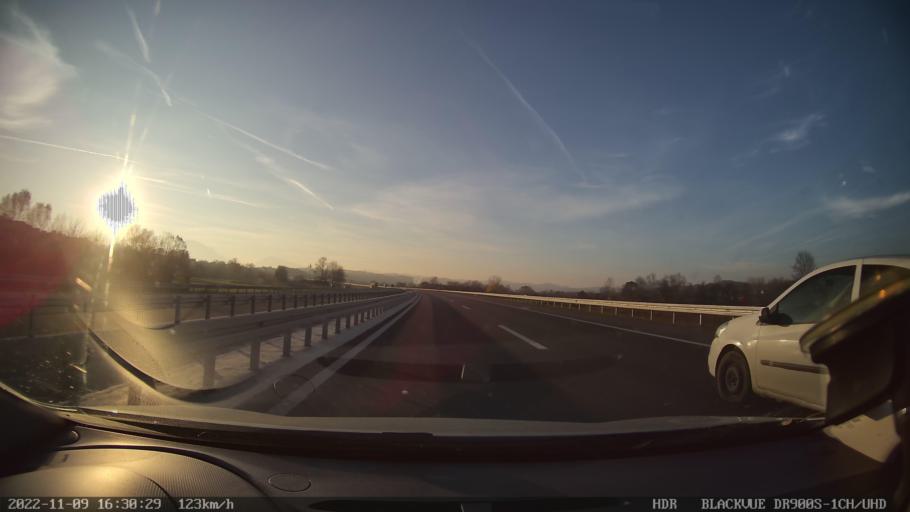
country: RS
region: Central Serbia
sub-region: Moravicki Okrug
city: Cacak
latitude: 43.9291
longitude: 20.3354
